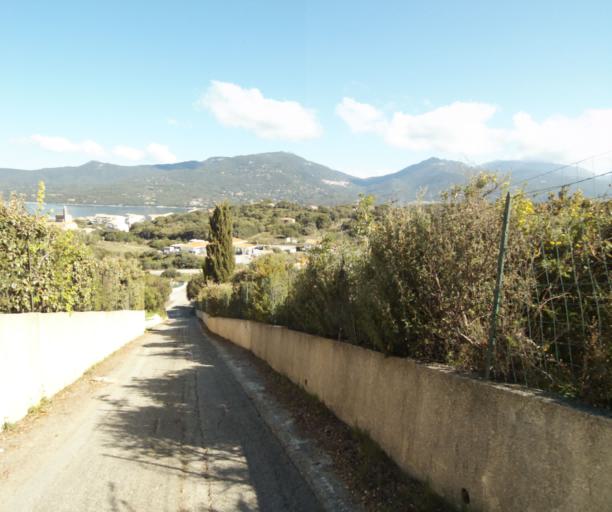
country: FR
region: Corsica
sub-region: Departement de la Corse-du-Sud
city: Propriano
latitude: 41.6696
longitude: 8.9094
